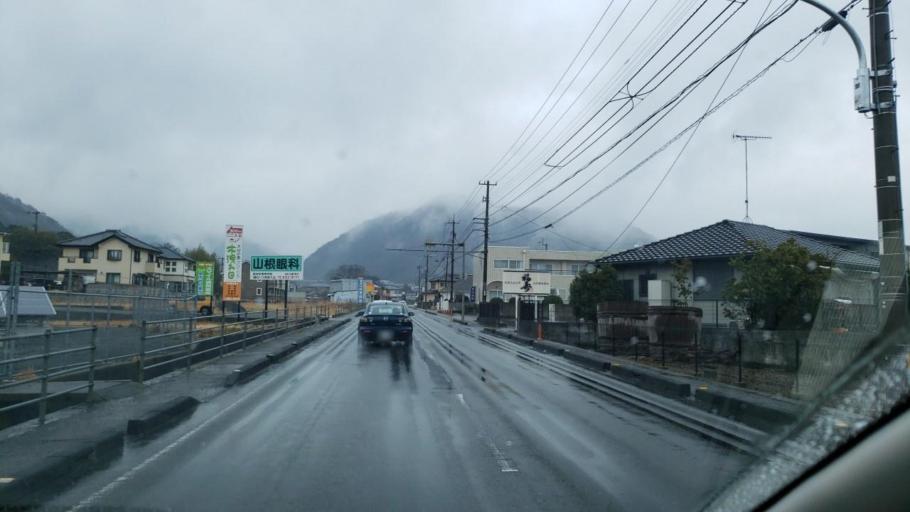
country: JP
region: Tokushima
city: Narutocho-mitsuishi
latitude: 34.1593
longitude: 134.5373
